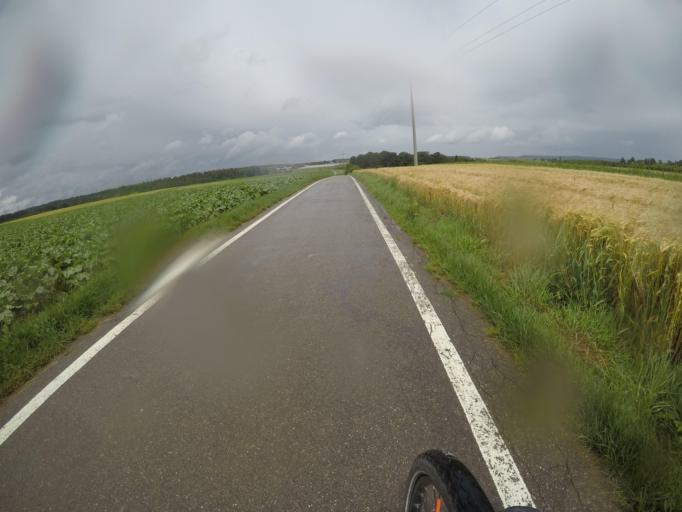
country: DE
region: Baden-Wuerttemberg
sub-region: Regierungsbezirk Stuttgart
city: Bondorf
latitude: 48.5334
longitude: 8.8220
